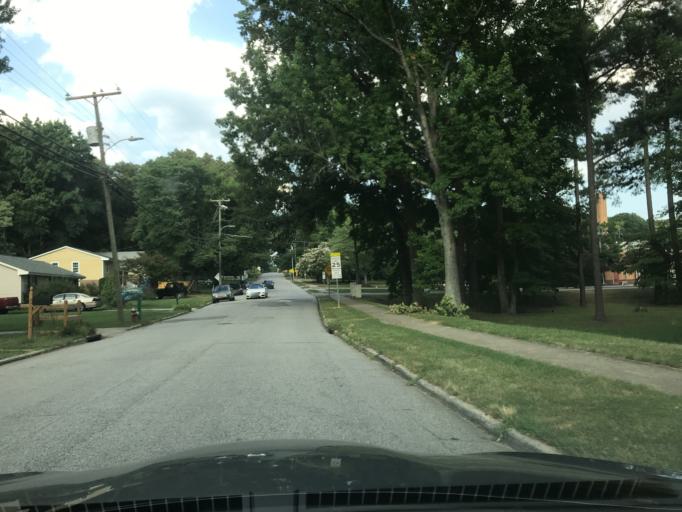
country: US
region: North Carolina
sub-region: Wake County
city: Raleigh
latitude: 35.8310
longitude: -78.5984
